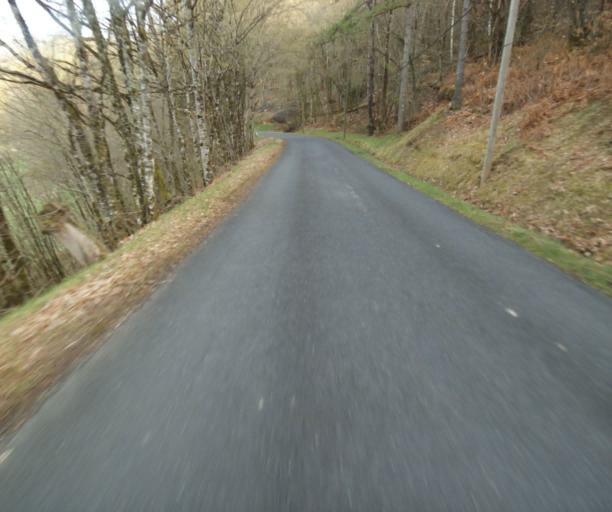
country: FR
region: Limousin
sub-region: Departement de la Correze
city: Correze
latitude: 45.3399
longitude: 1.8234
